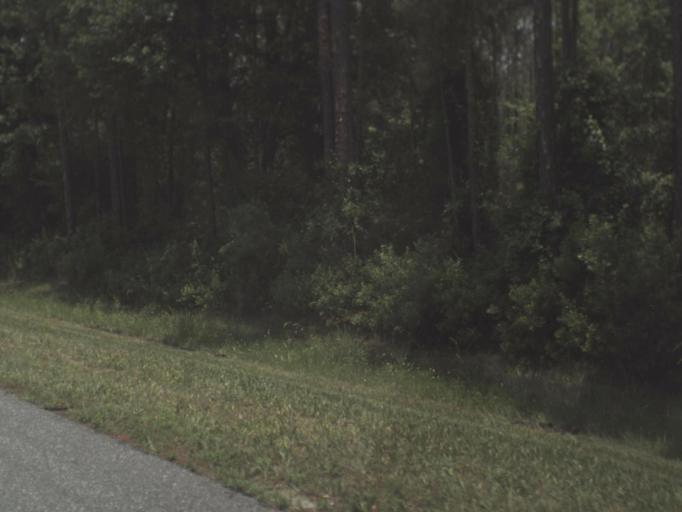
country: US
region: Florida
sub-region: Columbia County
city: Watertown
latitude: 30.1294
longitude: -82.5221
